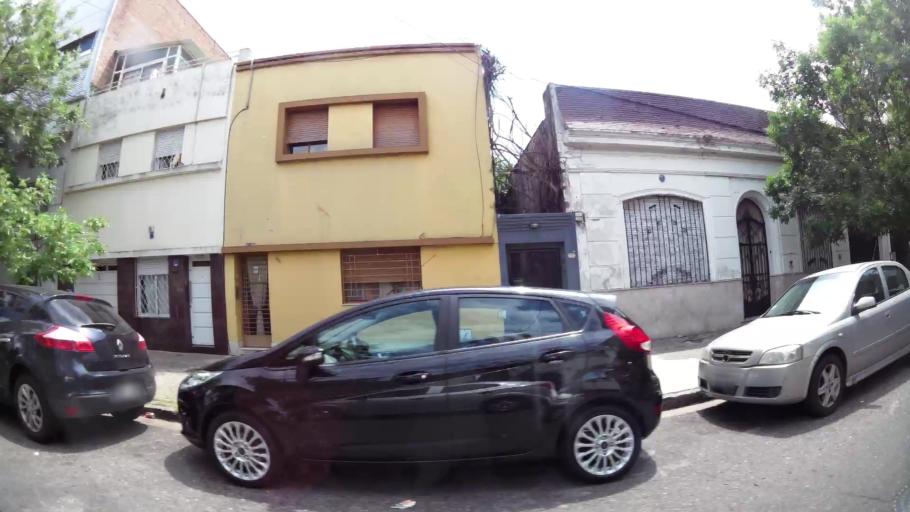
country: AR
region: Santa Fe
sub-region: Departamento de Rosario
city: Rosario
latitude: -32.9598
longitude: -60.6335
